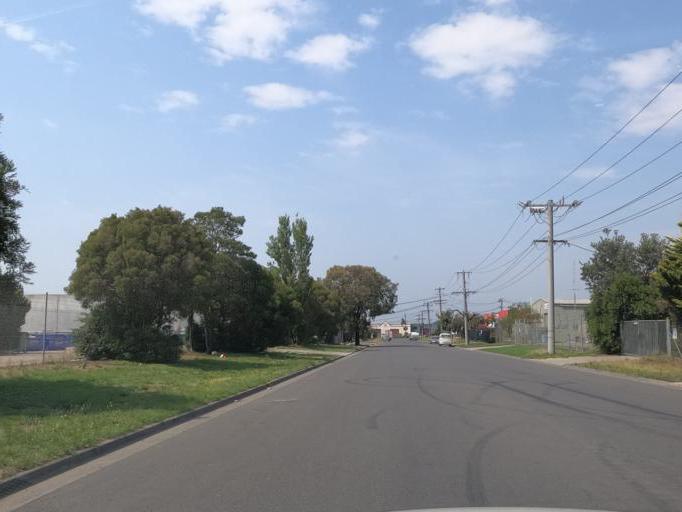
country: AU
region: Victoria
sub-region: Hume
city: Coolaroo
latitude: -37.6452
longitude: 144.9412
